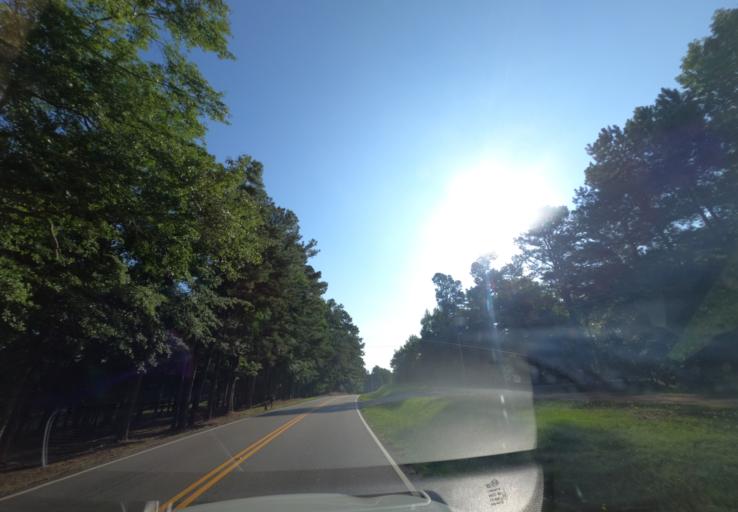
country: US
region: South Carolina
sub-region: Edgefield County
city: Murphys Estates
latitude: 33.5693
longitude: -82.0080
